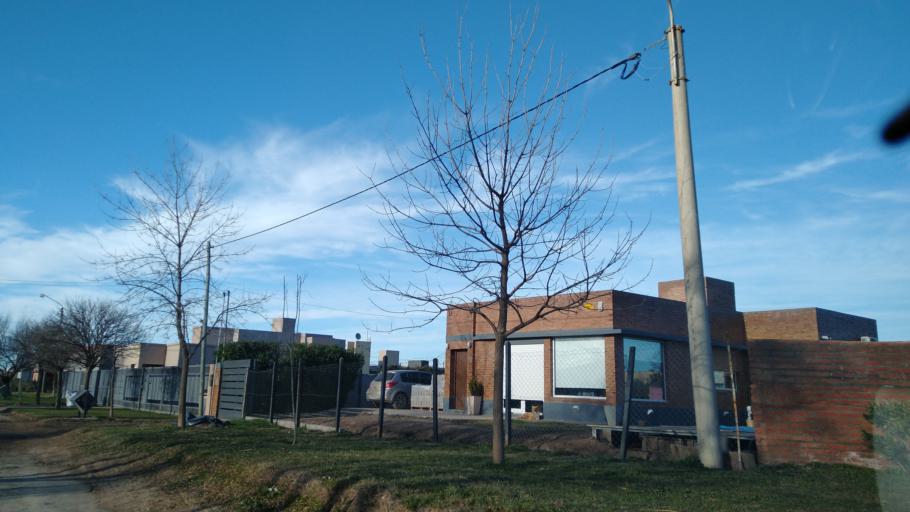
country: AR
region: Buenos Aires
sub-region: Partido de Bahia Blanca
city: Bahia Blanca
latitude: -38.7051
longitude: -62.2065
